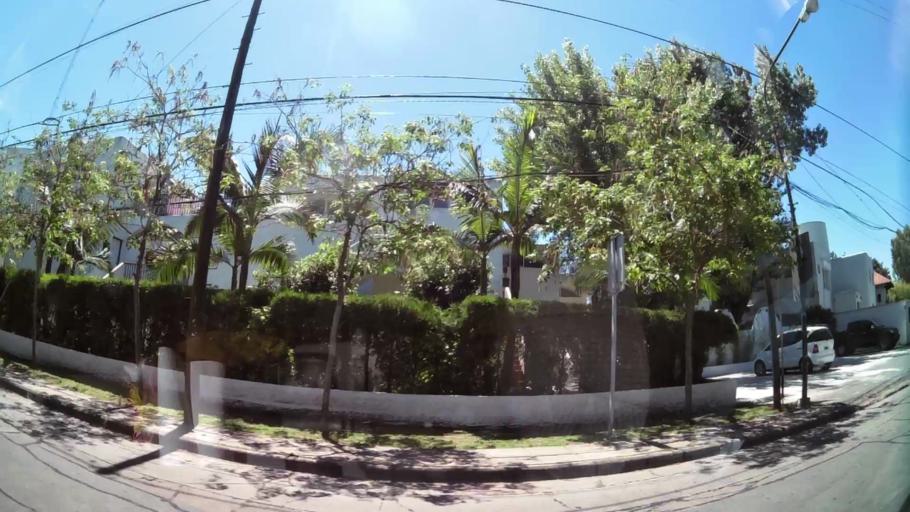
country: AR
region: Buenos Aires
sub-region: Partido de San Isidro
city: San Isidro
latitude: -34.4563
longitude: -58.5169
